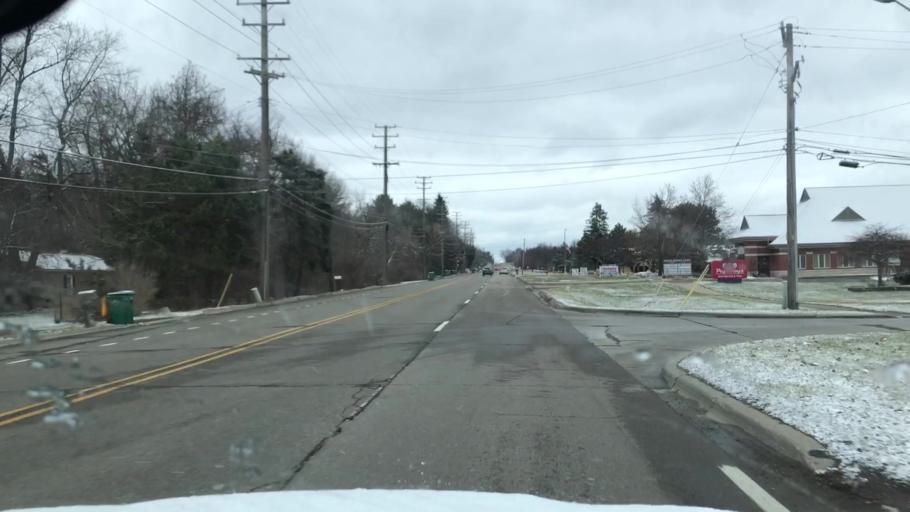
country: US
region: Michigan
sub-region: Wayne County
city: Northville
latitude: 42.4461
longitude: -83.4737
